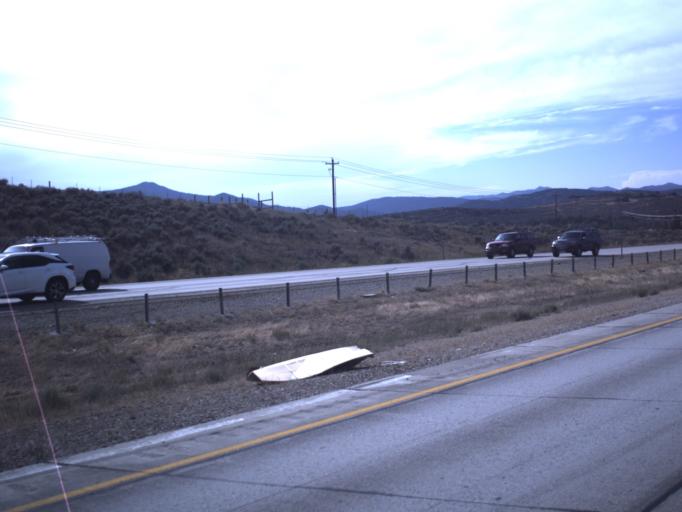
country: US
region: Utah
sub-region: Summit County
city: Snyderville
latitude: 40.7095
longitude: -111.4804
